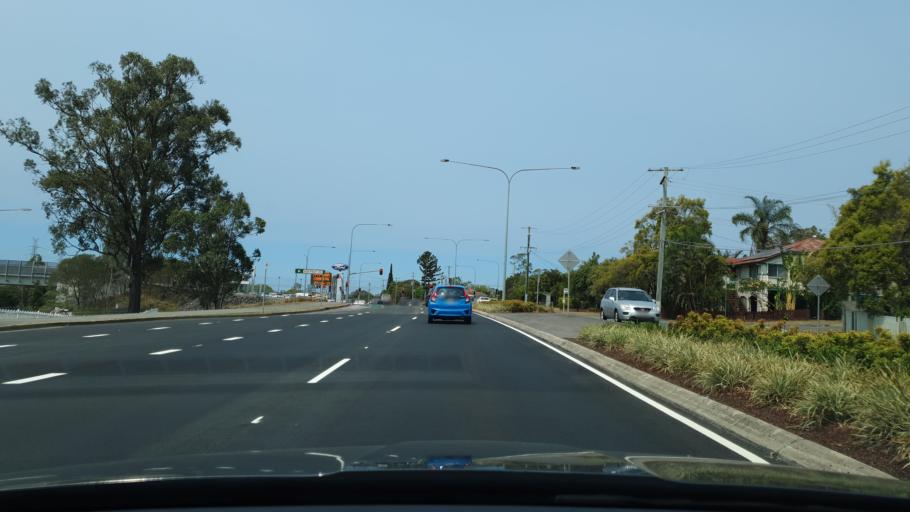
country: AU
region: Queensland
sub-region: Ipswich
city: Bundamba
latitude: -27.6035
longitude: 152.8227
